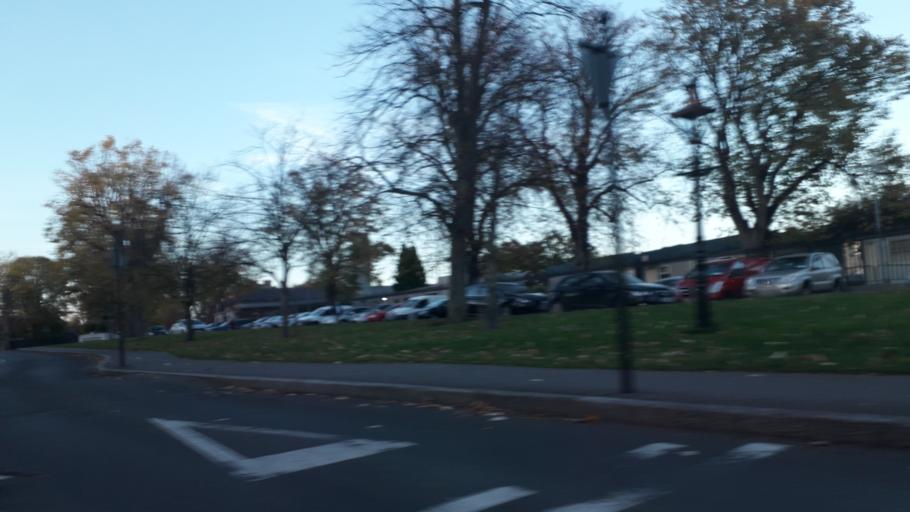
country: IE
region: Leinster
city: Cabra
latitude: 53.3529
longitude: -6.3012
